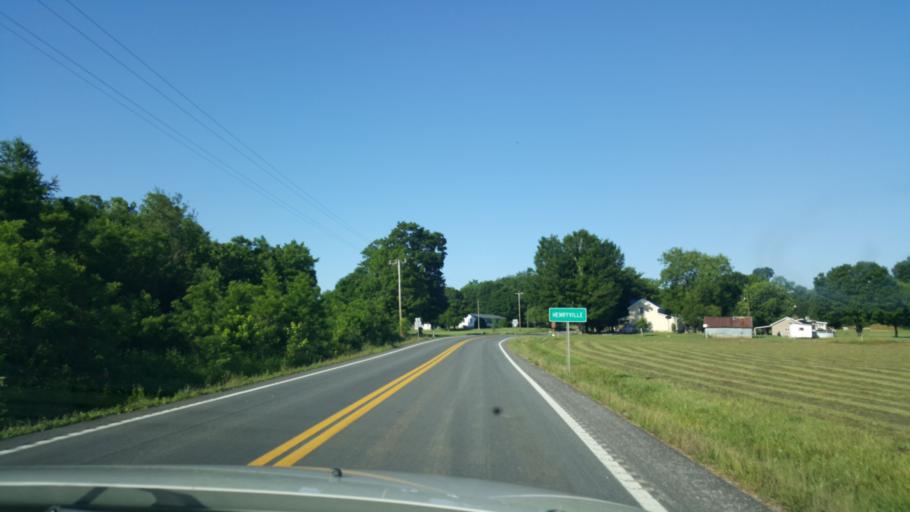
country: US
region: Tennessee
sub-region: Lawrence County
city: Lawrenceburg
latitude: 35.3941
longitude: -87.3909
